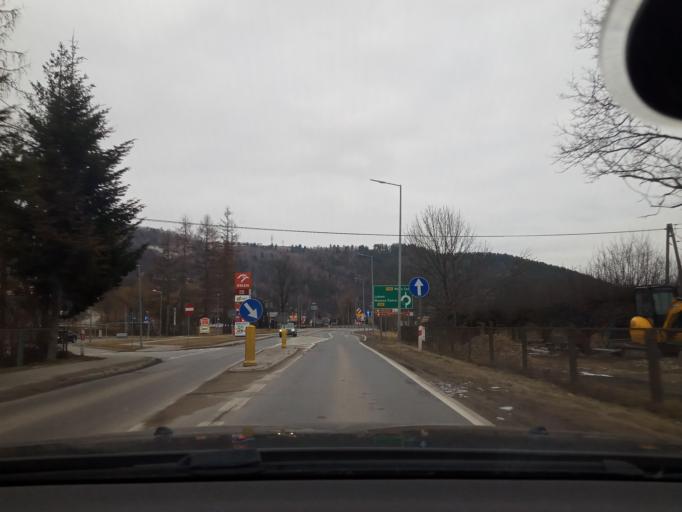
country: PL
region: Lesser Poland Voivodeship
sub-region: Powiat nowosadecki
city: Lacko
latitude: 49.5438
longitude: 20.4046
